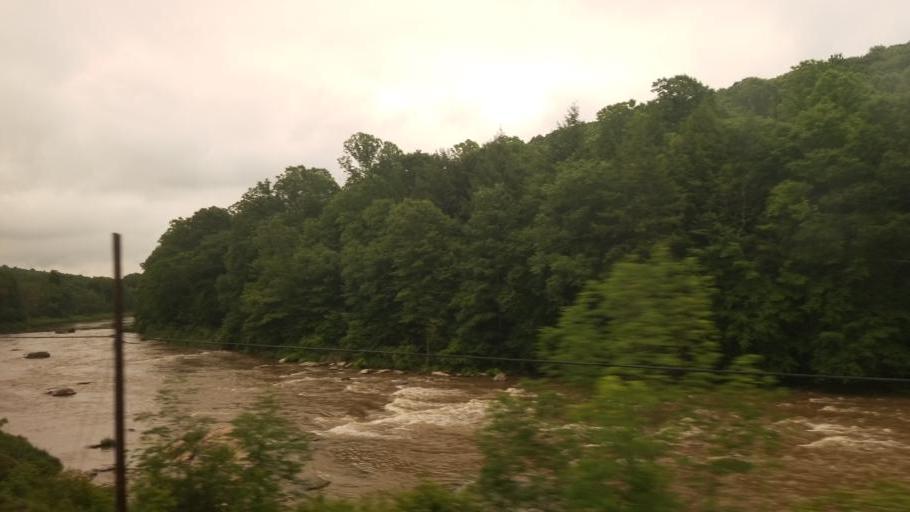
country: US
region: Pennsylvania
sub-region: Somerset County
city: Milford
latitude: 39.9078
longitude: -79.1857
